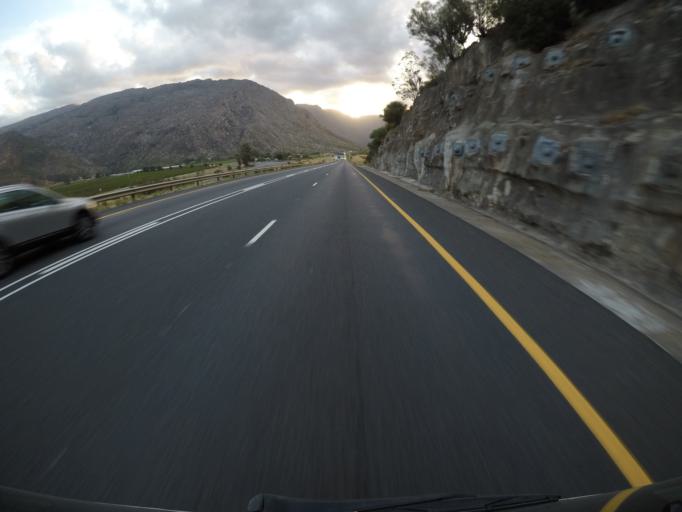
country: ZA
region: Western Cape
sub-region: Cape Winelands District Municipality
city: Worcester
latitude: -33.7050
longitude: 19.2526
